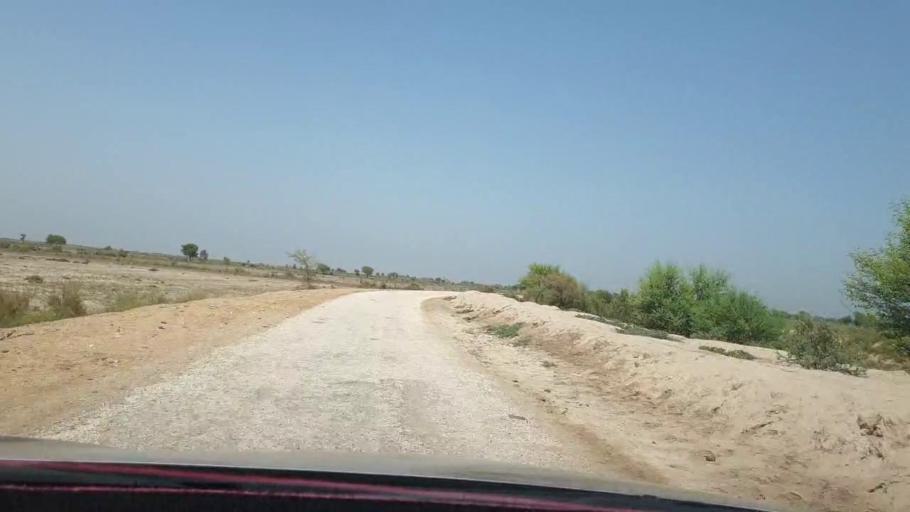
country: PK
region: Sindh
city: Warah
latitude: 27.5112
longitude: 67.7046
